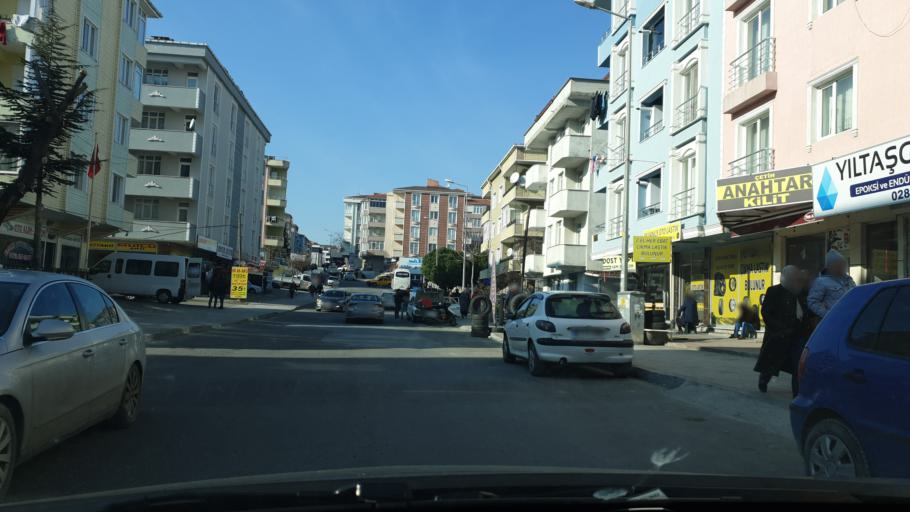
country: TR
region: Tekirdag
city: Cerkezkoey
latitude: 41.2824
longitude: 27.9959
